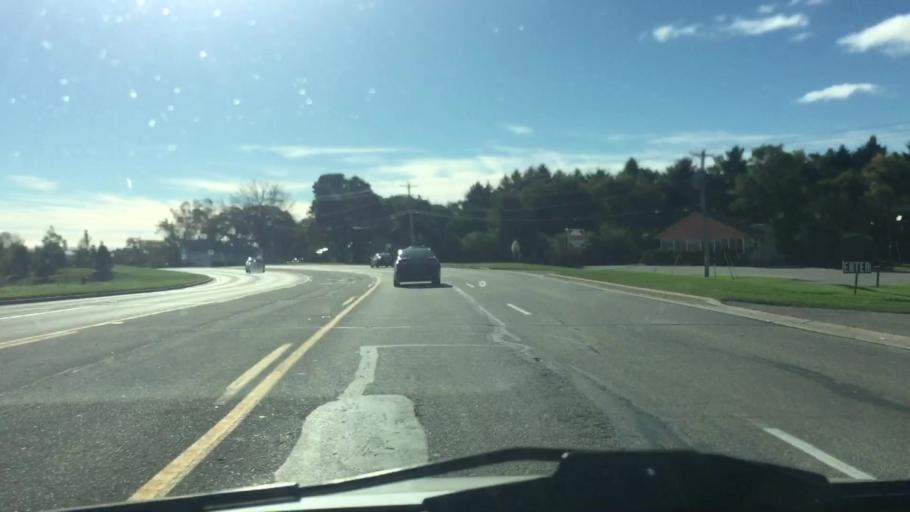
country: US
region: Wisconsin
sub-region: Waukesha County
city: Waukesha
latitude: 43.0409
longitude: -88.2229
